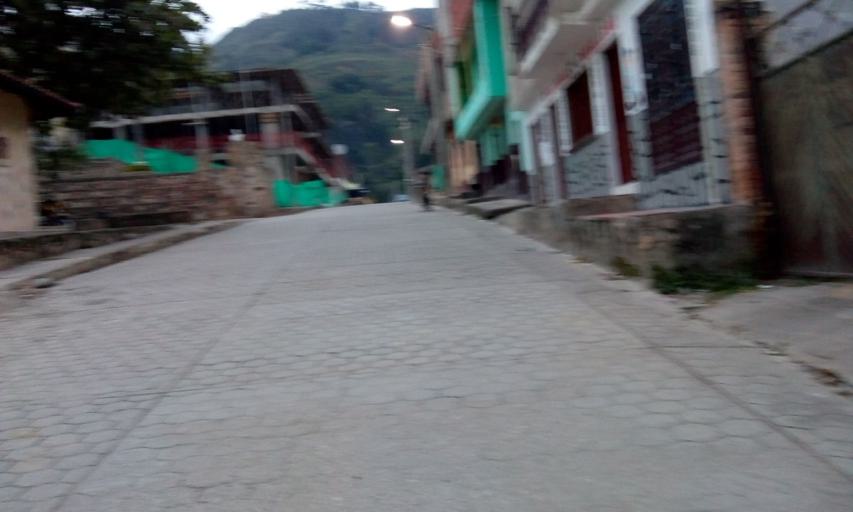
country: CO
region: Boyaca
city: Tipacoque
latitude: 6.4213
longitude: -72.6911
